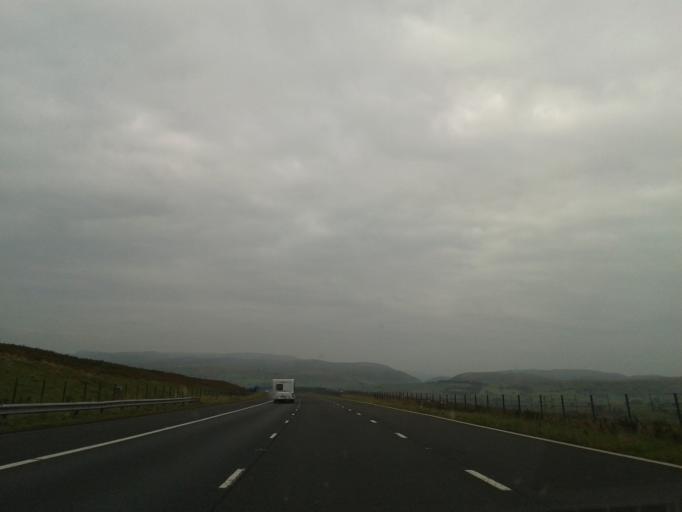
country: GB
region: England
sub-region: Cumbria
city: Appleby-in-Westmorland
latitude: 54.4707
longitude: -2.6282
